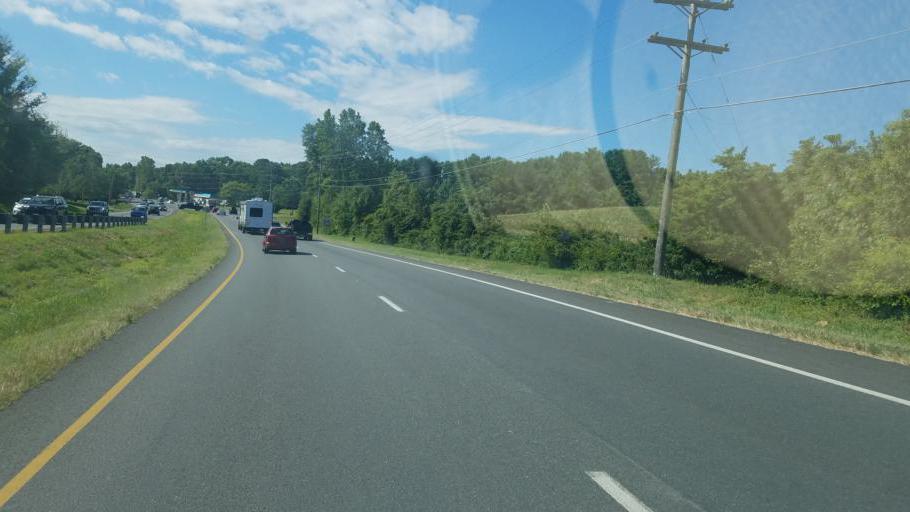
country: US
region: Virginia
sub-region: Fauquier County
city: Warrenton
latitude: 38.6450
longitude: -77.8048
